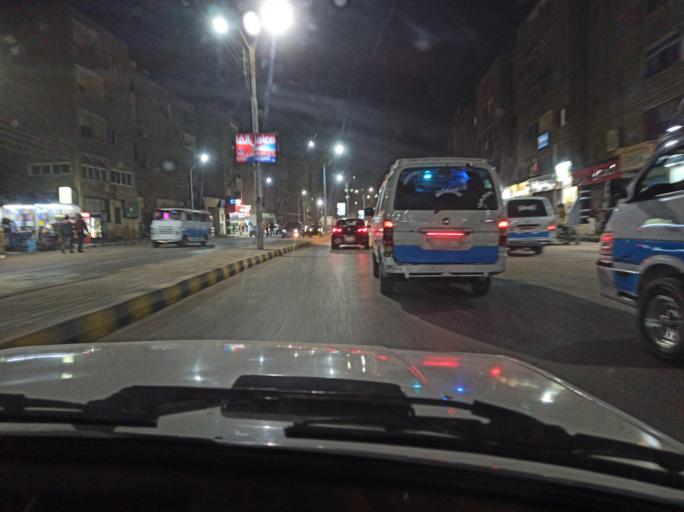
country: EG
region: Muhafazat Bani Suwayf
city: Bani Suwayf
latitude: 29.0720
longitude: 31.1096
